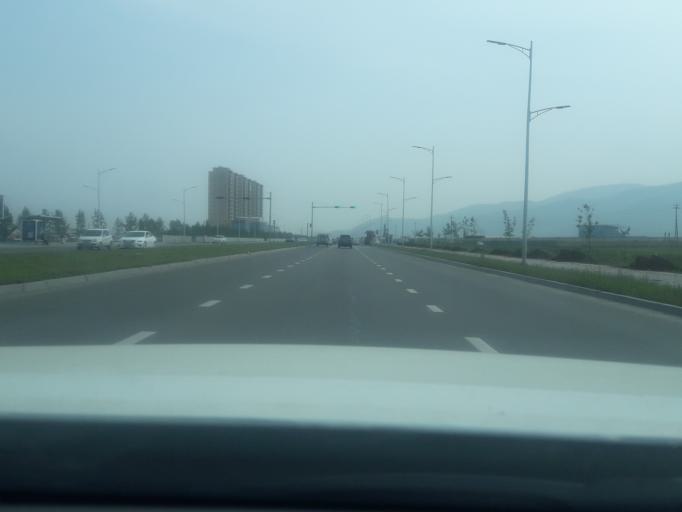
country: MN
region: Ulaanbaatar
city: Ulaanbaatar
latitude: 47.8613
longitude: 106.7985
